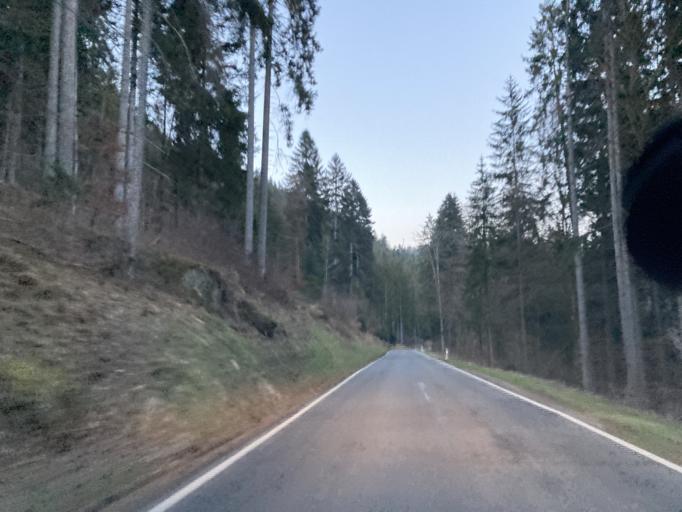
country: DE
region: Baden-Wuerttemberg
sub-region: Karlsruhe Region
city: Bad Teinach-Zavelstein
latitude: 48.6792
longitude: 8.6633
